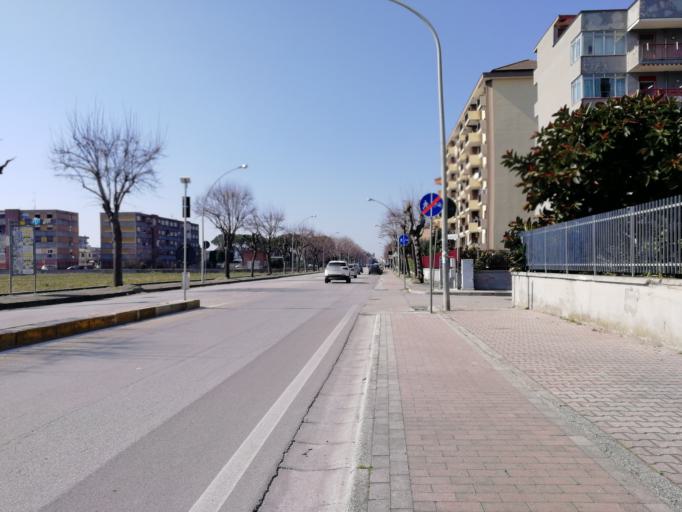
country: IT
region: Campania
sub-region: Provincia di Caserta
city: Santa Maria Capua Vetere
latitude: 41.0900
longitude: 14.2631
